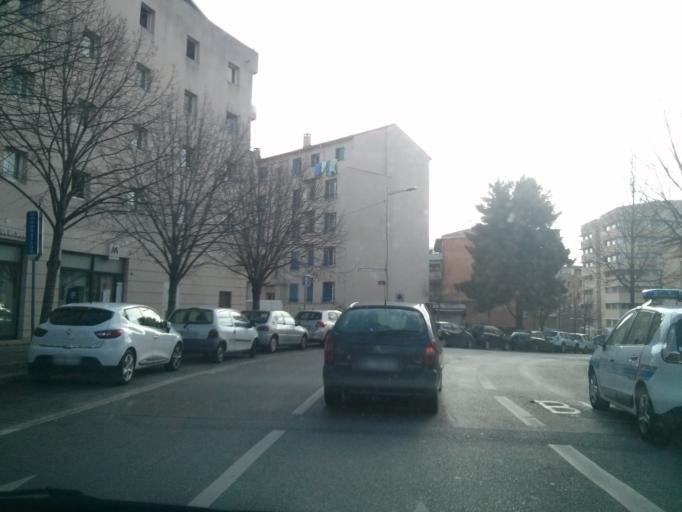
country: FR
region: Provence-Alpes-Cote d'Azur
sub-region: Departement des Bouches-du-Rhone
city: Aix-en-Provence
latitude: 43.5288
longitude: 5.4391
